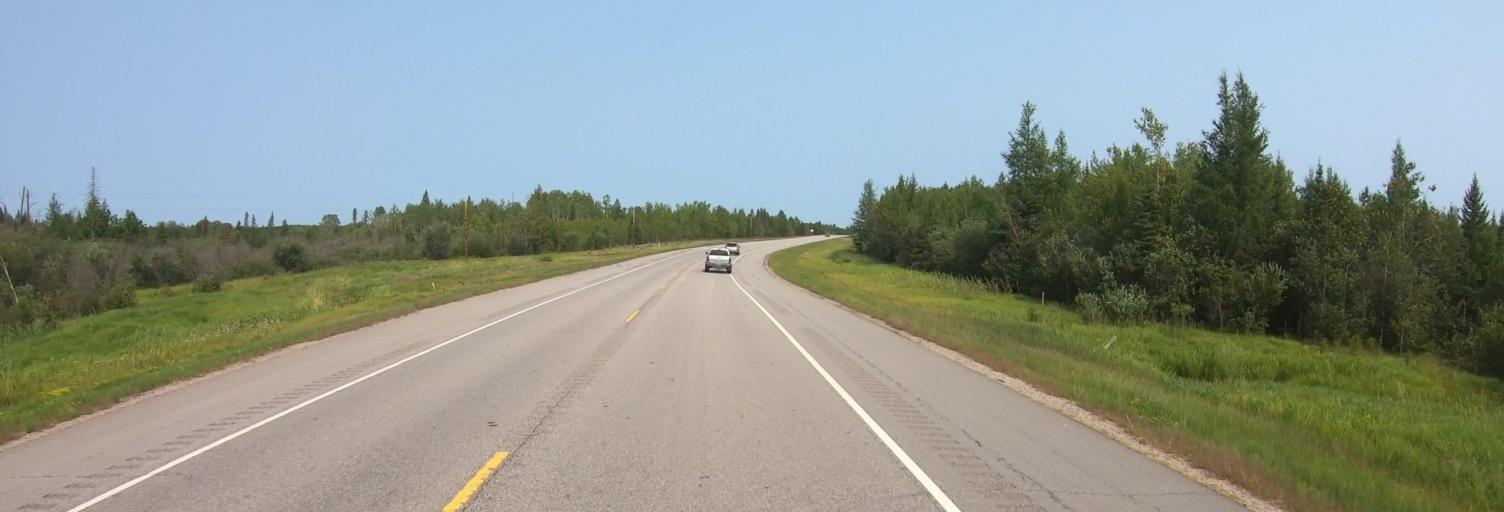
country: CA
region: Ontario
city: Fort Frances
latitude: 48.3300
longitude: -92.9623
